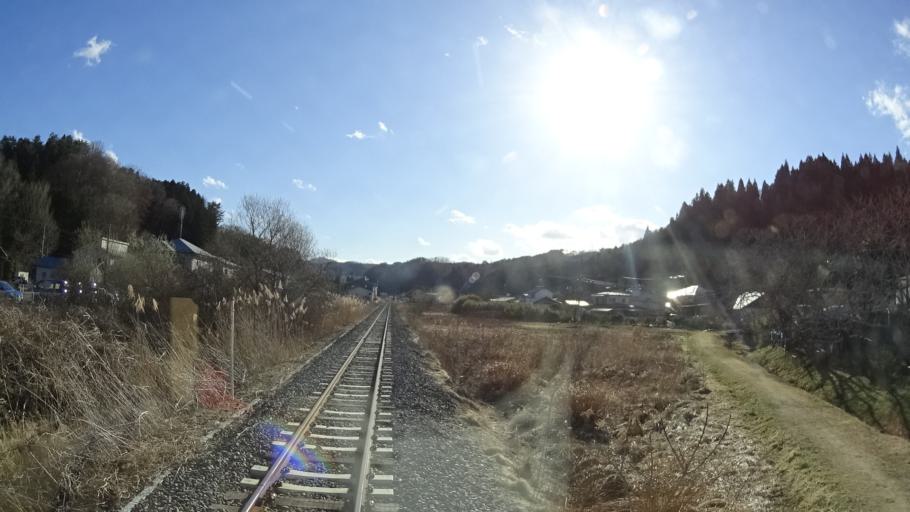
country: JP
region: Iwate
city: Miyako
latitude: 39.6179
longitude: 141.9444
